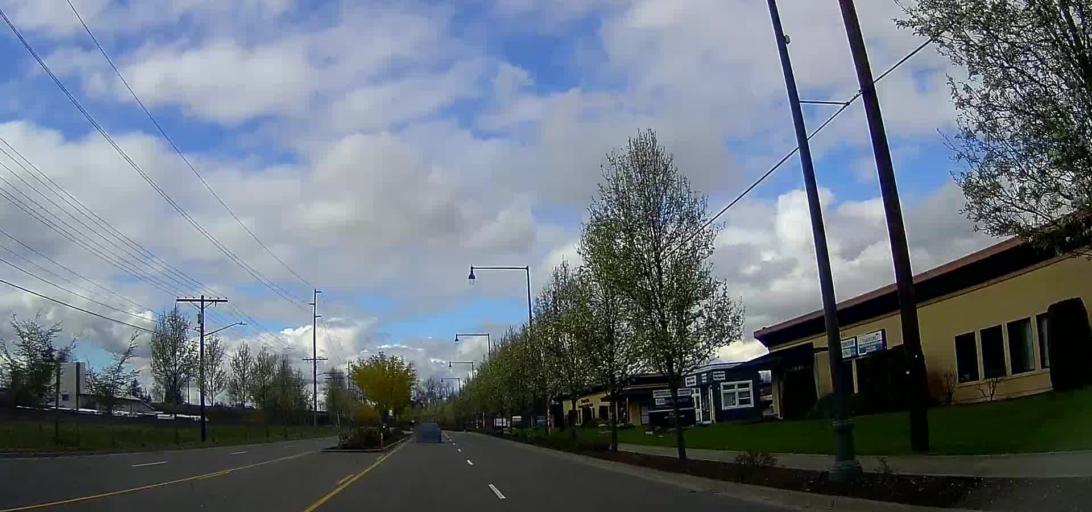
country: US
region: Washington
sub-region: Snohomish County
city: Smokey Point
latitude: 48.1202
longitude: -122.1825
